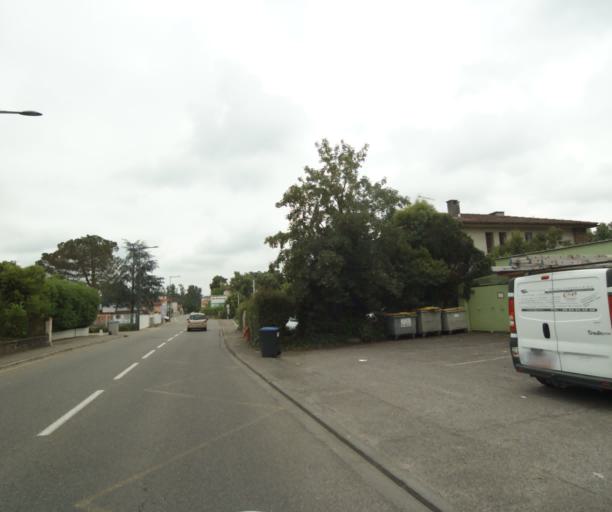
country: FR
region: Midi-Pyrenees
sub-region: Departement du Tarn-et-Garonne
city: Montauban
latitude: 44.0114
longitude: 1.3544
